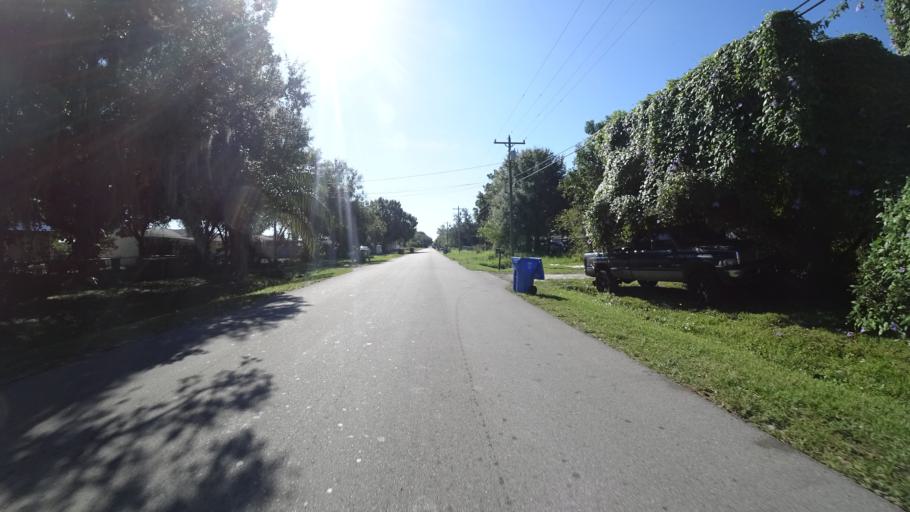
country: US
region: Florida
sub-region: Hillsborough County
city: Sun City Center
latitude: 27.6552
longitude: -82.3538
